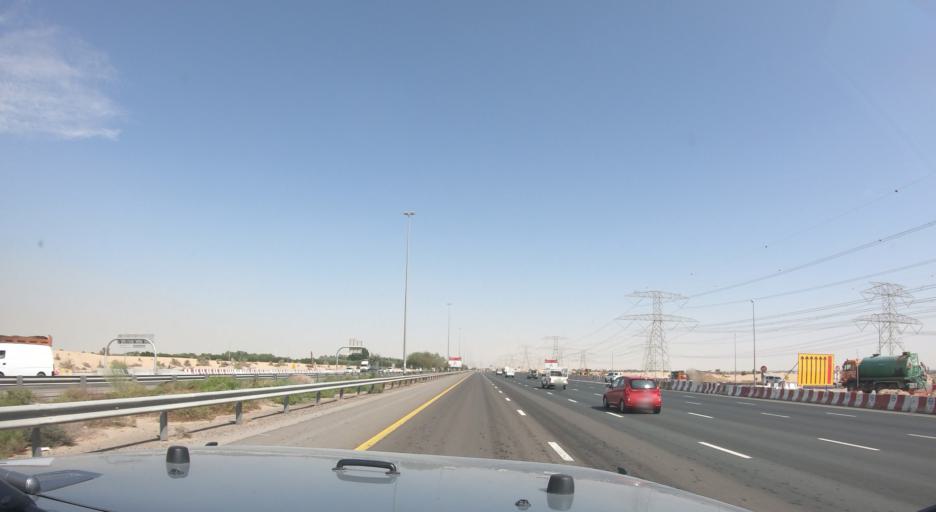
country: AE
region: Ash Shariqah
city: Sharjah
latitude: 25.1843
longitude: 55.5235
